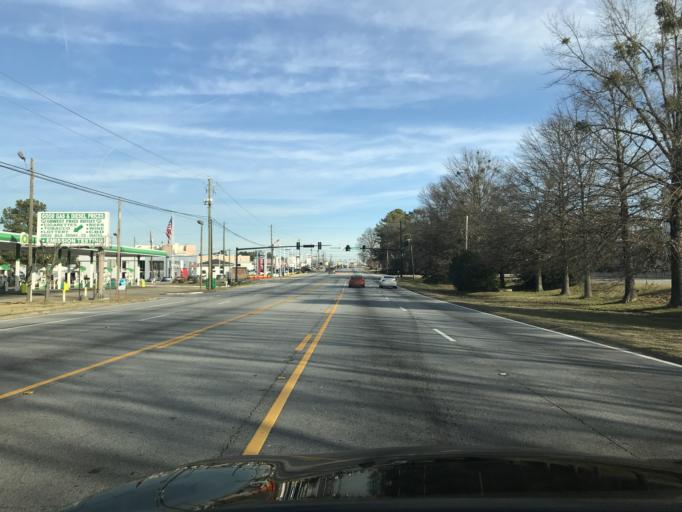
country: US
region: Georgia
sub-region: Clayton County
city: Morrow
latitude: 33.5652
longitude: -84.3442
